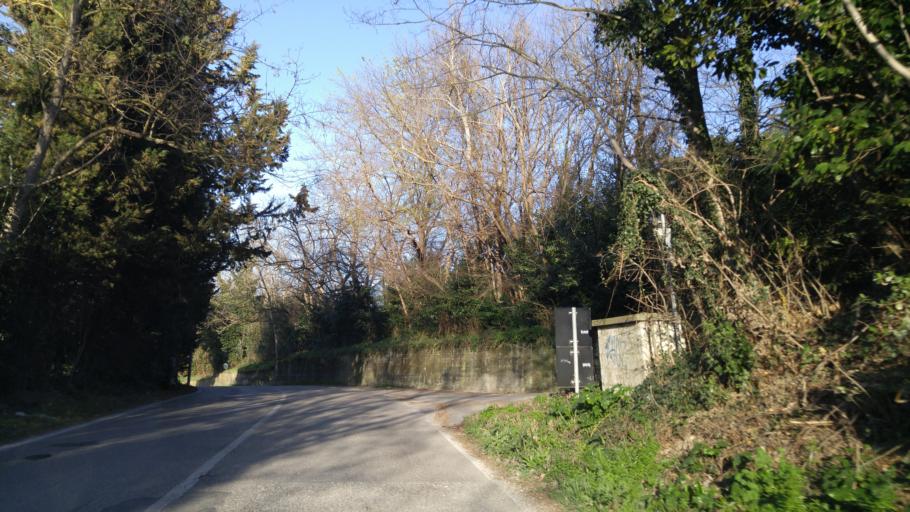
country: IT
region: The Marches
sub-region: Provincia di Pesaro e Urbino
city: Pesaro
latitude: 43.8823
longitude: 12.9054
